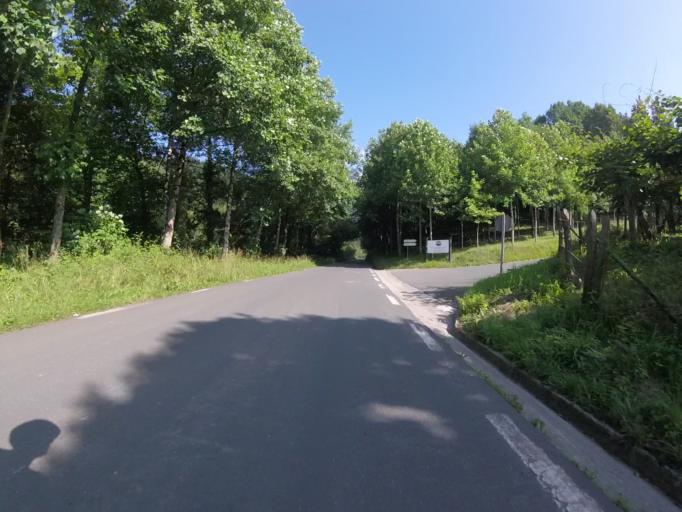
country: ES
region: Basque Country
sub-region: Provincia de Guipuzcoa
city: Ormaiztegui
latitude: 43.0552
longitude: -2.2356
